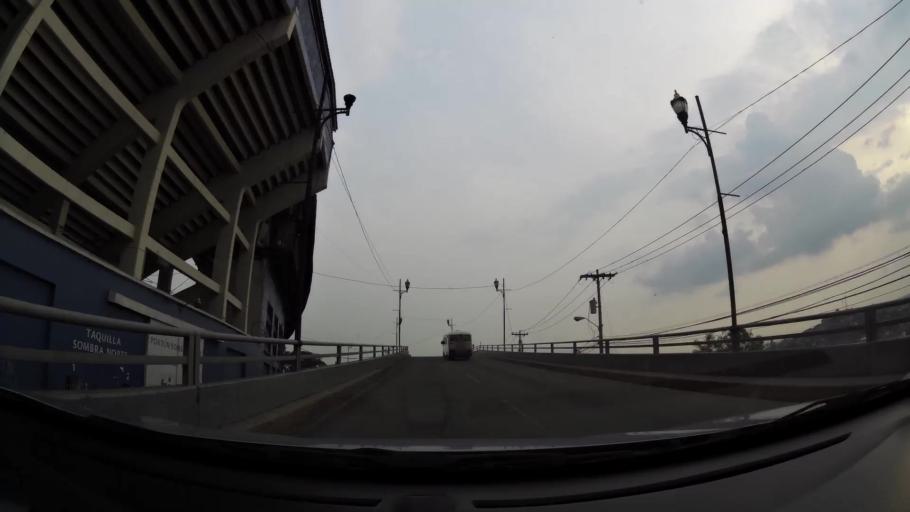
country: HN
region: Francisco Morazan
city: Tegucigalpa
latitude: 14.0997
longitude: -87.2042
